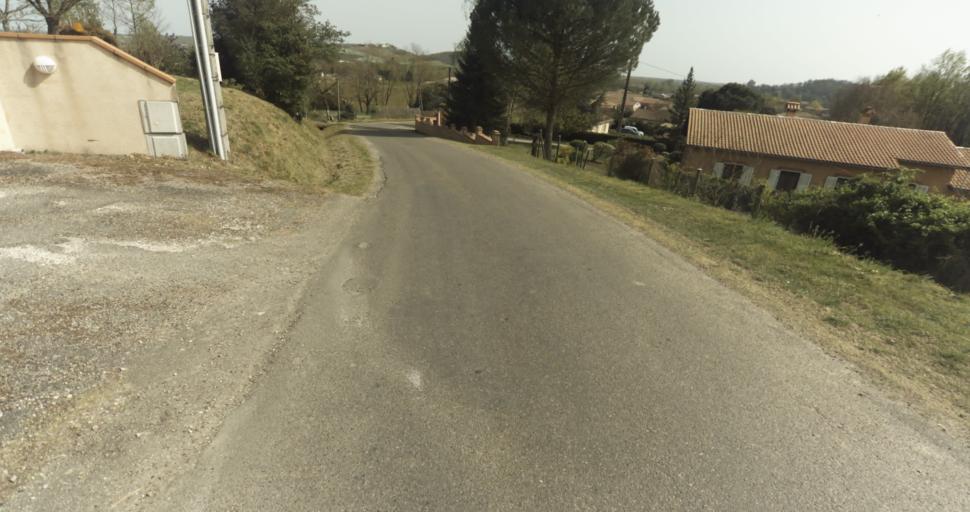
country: FR
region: Midi-Pyrenees
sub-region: Departement du Tarn-et-Garonne
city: Moissac
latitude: 44.1295
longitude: 1.1486
